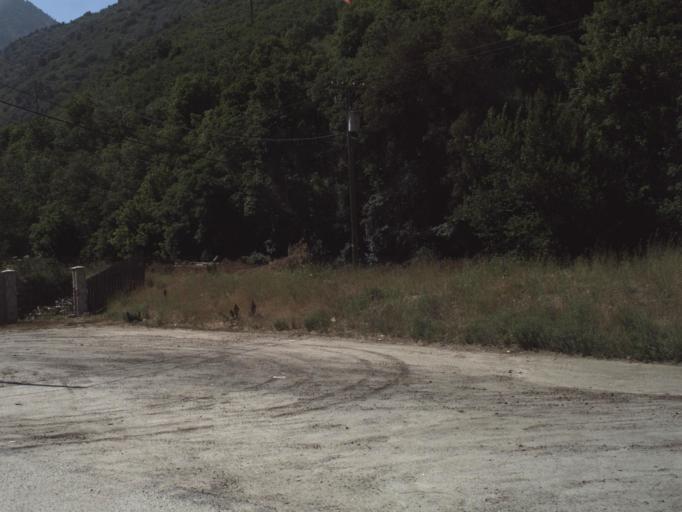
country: US
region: Utah
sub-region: Weber County
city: Liberty
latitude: 41.2540
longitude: -111.8484
